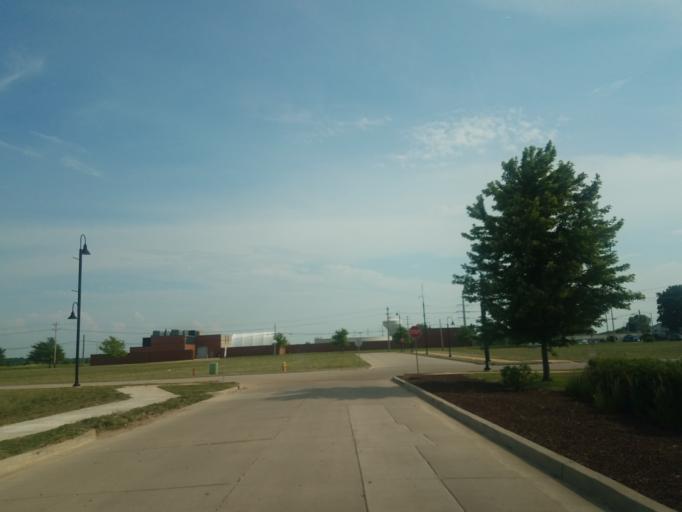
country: US
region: Illinois
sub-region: McLean County
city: Bloomington
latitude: 40.4605
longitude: -88.9613
